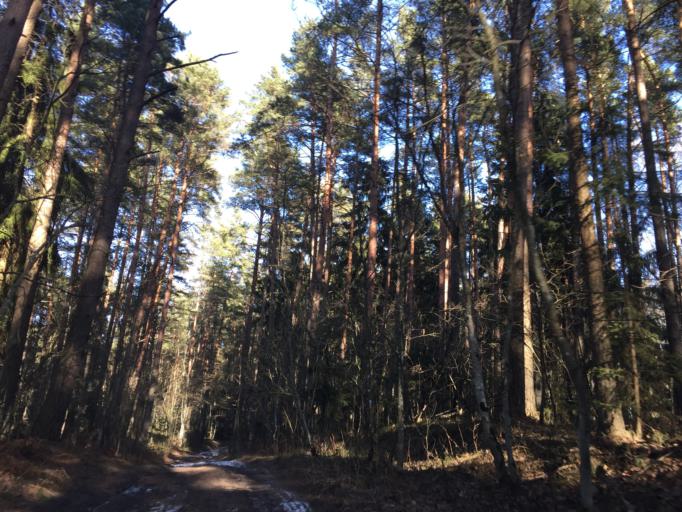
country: LV
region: Babite
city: Pinki
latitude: 56.9683
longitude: 23.8853
